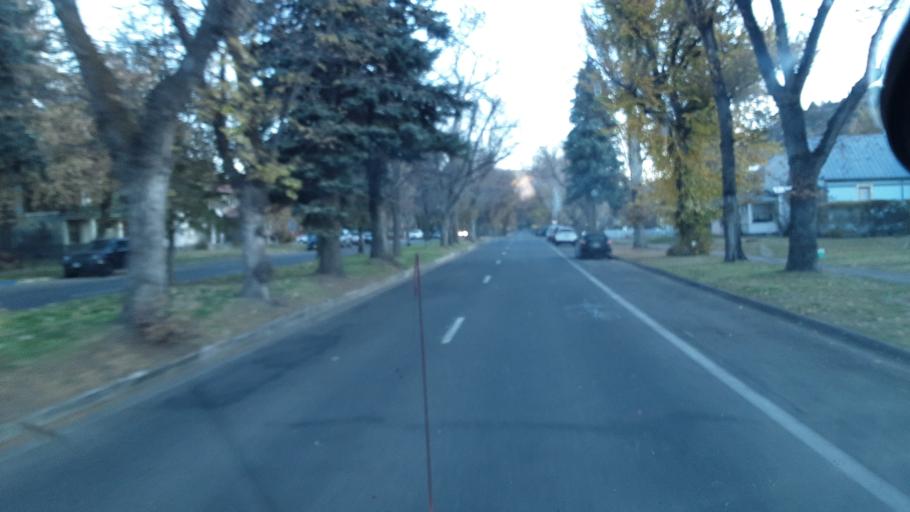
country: US
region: Colorado
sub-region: La Plata County
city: Durango
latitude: 37.2729
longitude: -107.8778
